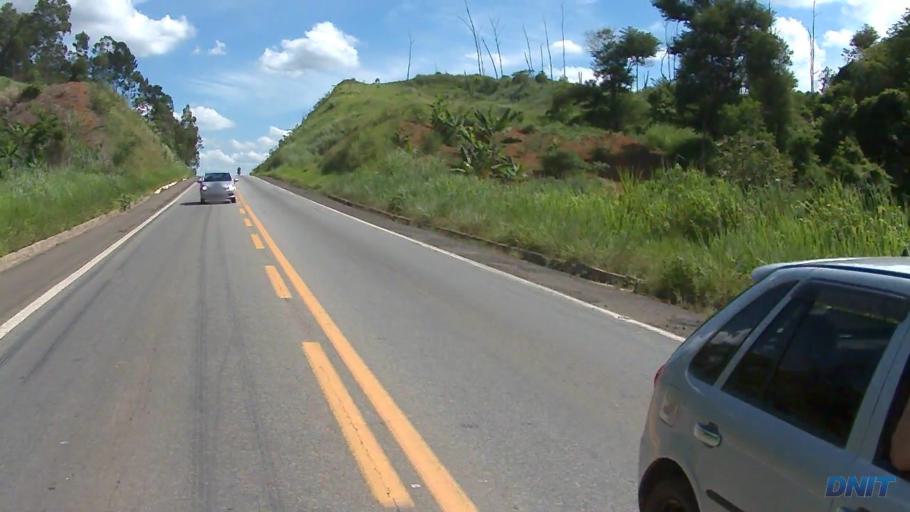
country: BR
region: Minas Gerais
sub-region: Ipatinga
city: Ipatinga
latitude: -19.4319
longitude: -42.5059
